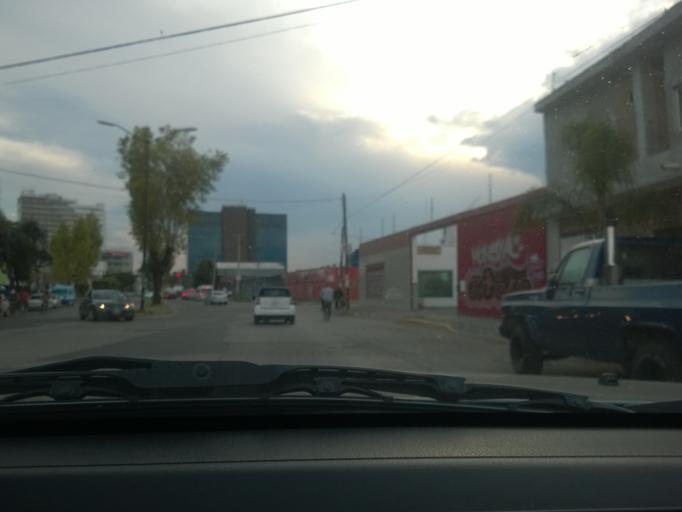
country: MX
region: Guanajuato
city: Leon
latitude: 21.1200
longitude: -101.6576
